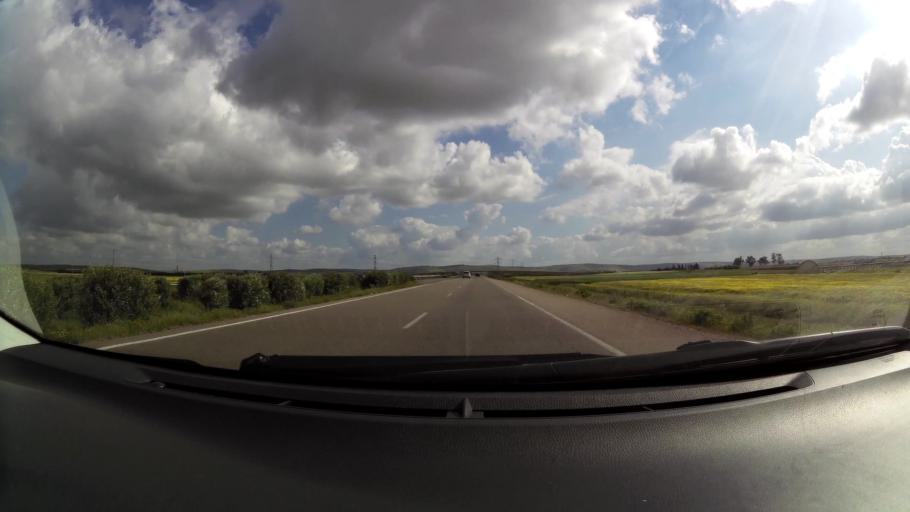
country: MA
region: Chaouia-Ouardigha
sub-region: Settat Province
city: Settat
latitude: 33.1198
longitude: -7.5805
